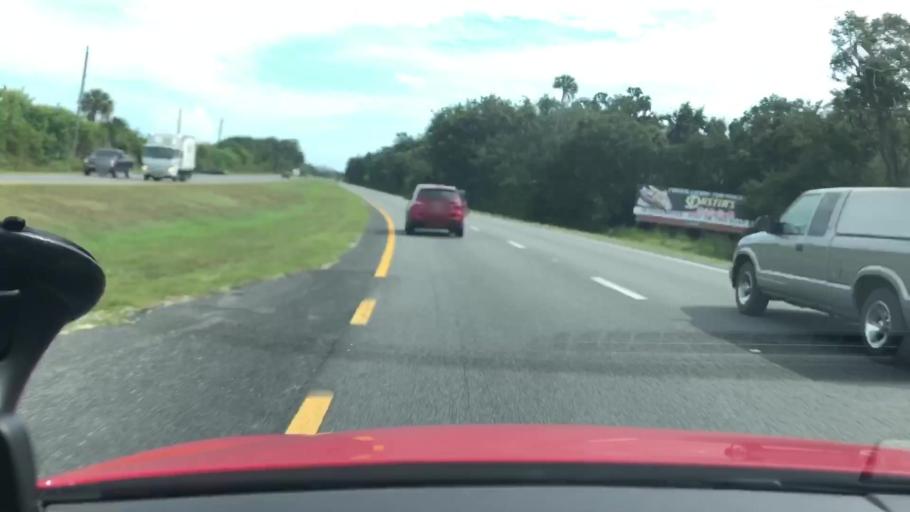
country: US
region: Florida
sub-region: Volusia County
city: Ponce Inlet
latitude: 29.0826
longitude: -80.9652
